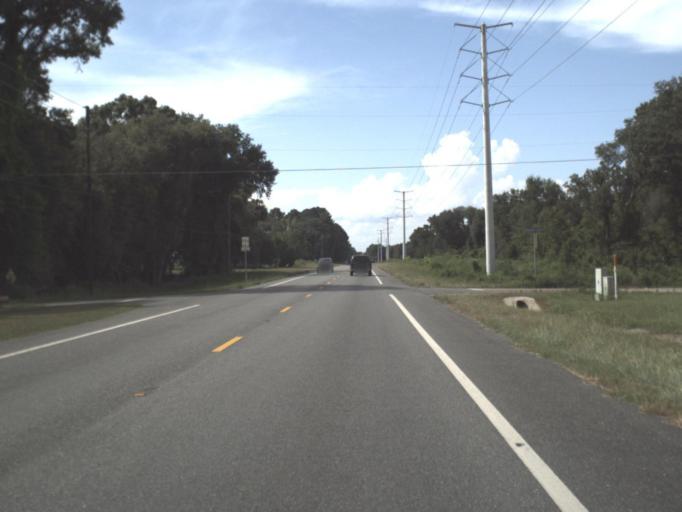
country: US
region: Florida
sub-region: Taylor County
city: Perry
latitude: 30.1498
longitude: -83.5900
